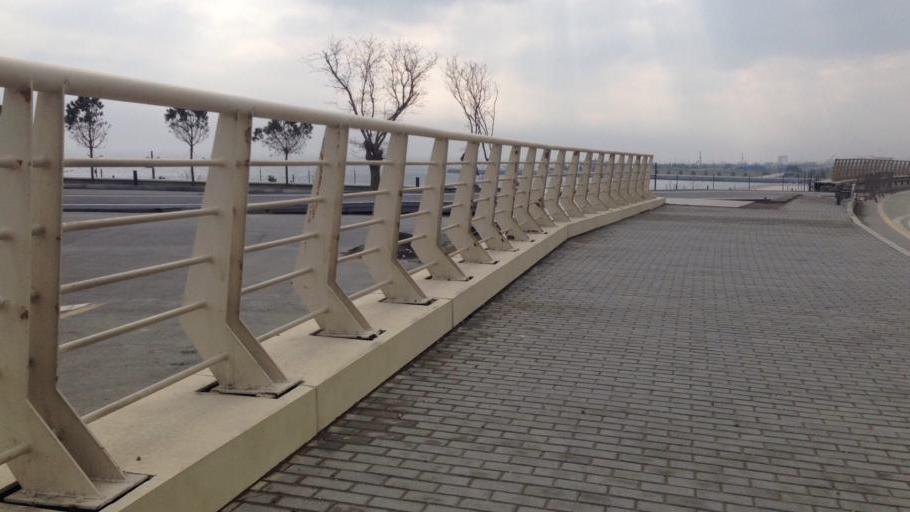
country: AZ
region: Baki
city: Badamdar
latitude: 40.3434
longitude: 49.8429
